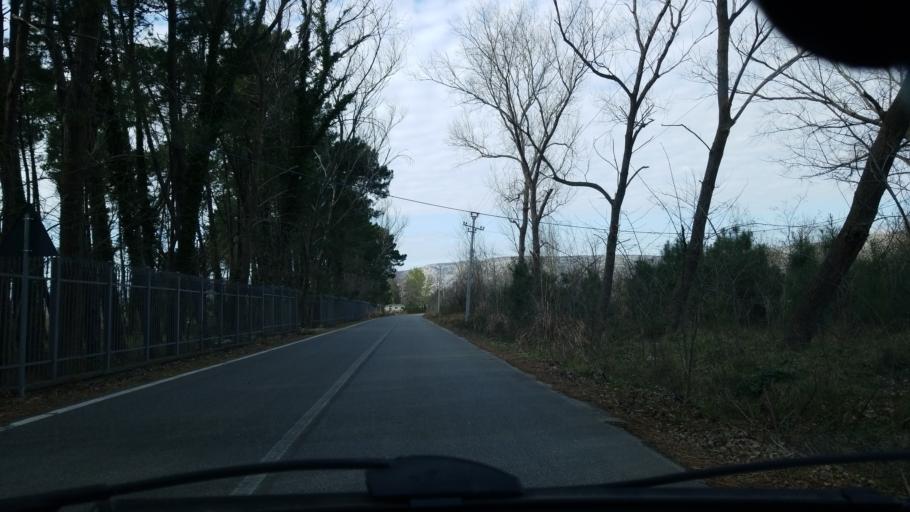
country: AL
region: Lezhe
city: Shengjin
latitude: 41.7820
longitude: 19.6038
